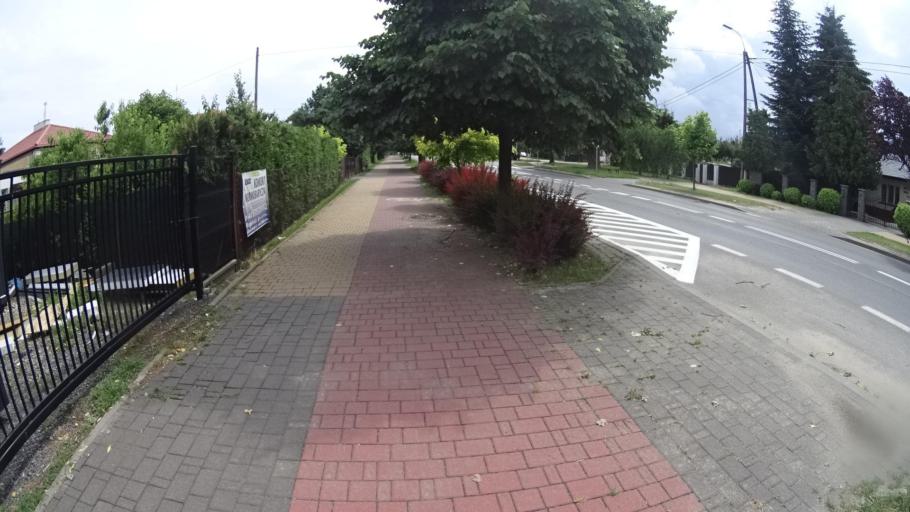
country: PL
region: Masovian Voivodeship
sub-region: Powiat grojecki
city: Grojec
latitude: 51.8580
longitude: 20.8693
